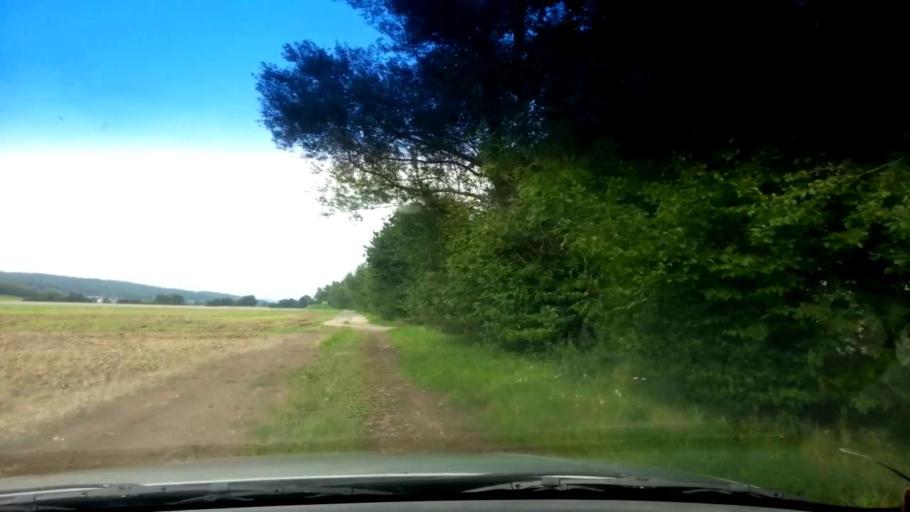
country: DE
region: Bavaria
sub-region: Upper Franconia
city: Zapfendorf
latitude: 50.0378
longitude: 10.9214
